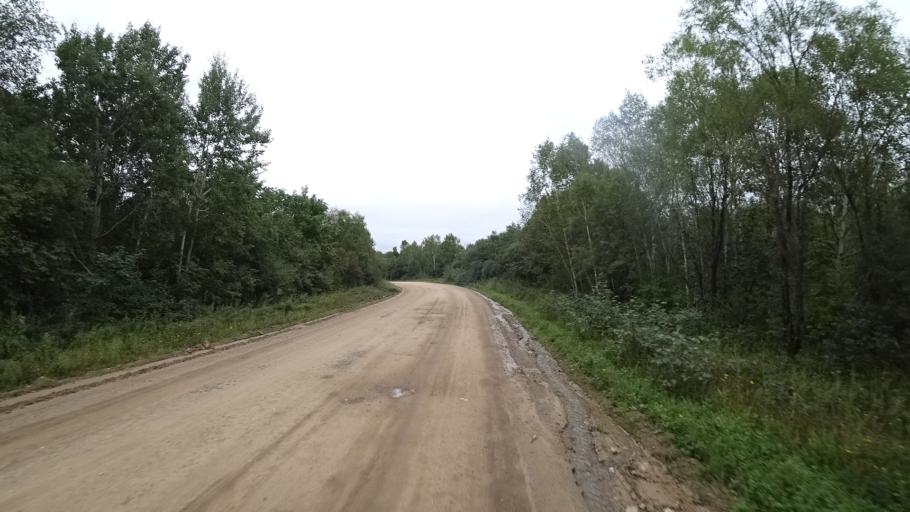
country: RU
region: Primorskiy
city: Rettikhovka
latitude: 44.1759
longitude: 132.8013
